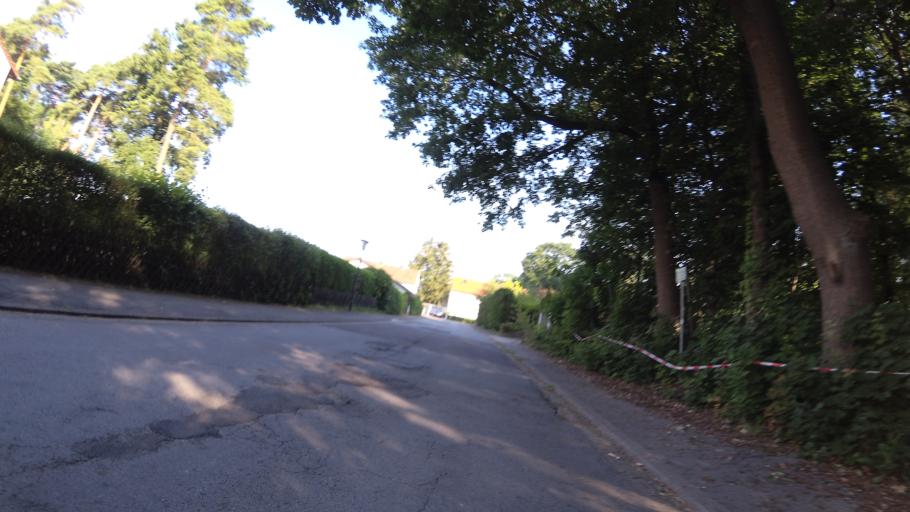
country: DE
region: Saarland
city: Homburg
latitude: 49.3322
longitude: 7.3228
